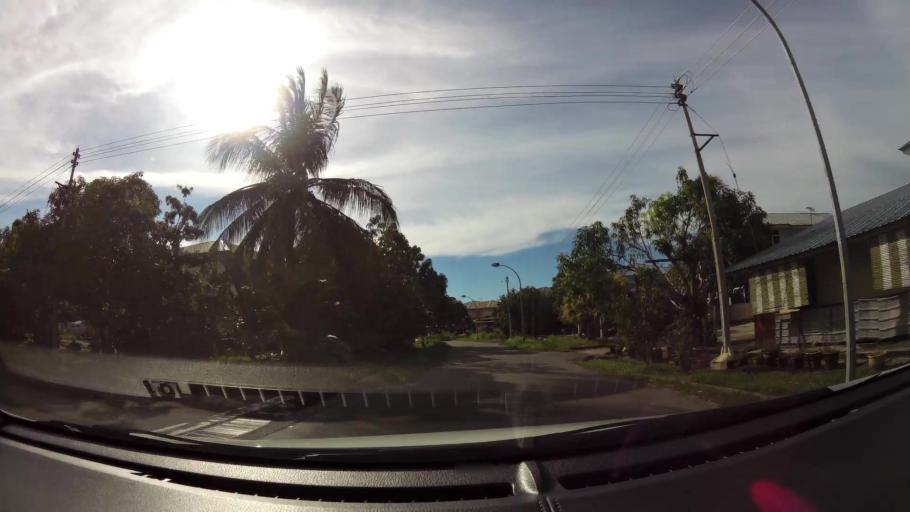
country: BN
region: Brunei and Muara
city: Bandar Seri Begawan
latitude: 4.9723
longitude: 115.0295
